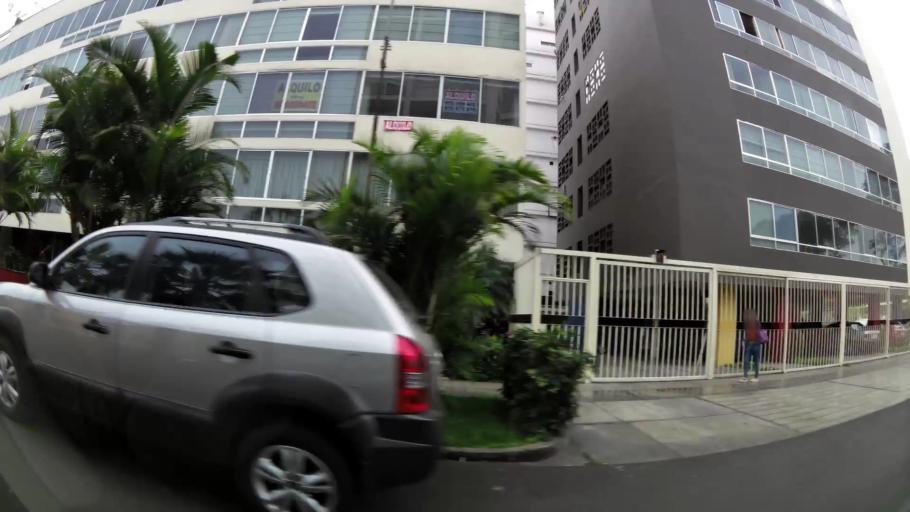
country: PE
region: Lima
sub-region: Lima
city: San Isidro
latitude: -12.1032
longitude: -77.0481
